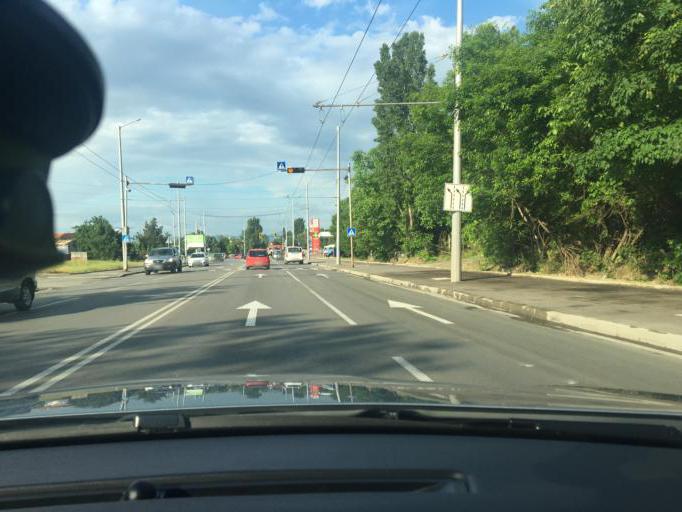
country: BG
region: Sofia-Capital
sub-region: Stolichna Obshtina
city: Sofia
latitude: 42.6736
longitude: 23.3743
